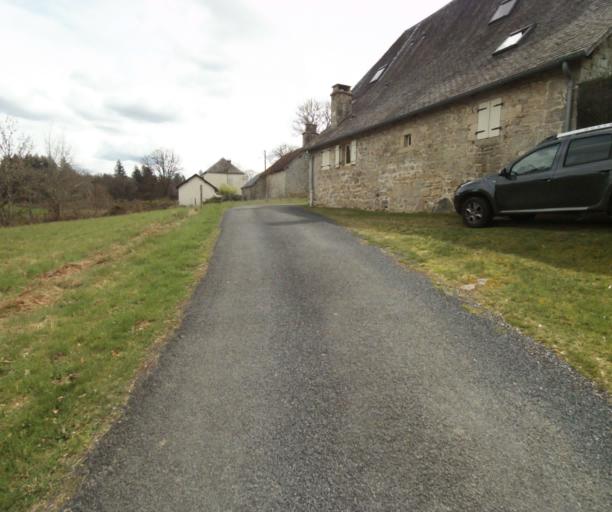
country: FR
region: Limousin
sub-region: Departement de la Correze
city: Argentat
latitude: 45.2219
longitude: 1.9199
